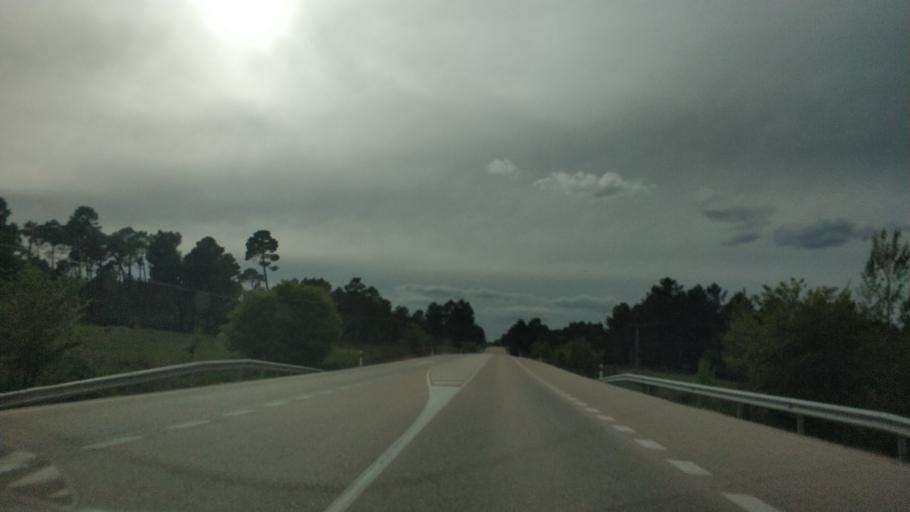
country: ES
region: Castille and Leon
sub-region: Provincia de Soria
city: Valdenebro
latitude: 41.5604
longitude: -2.9743
